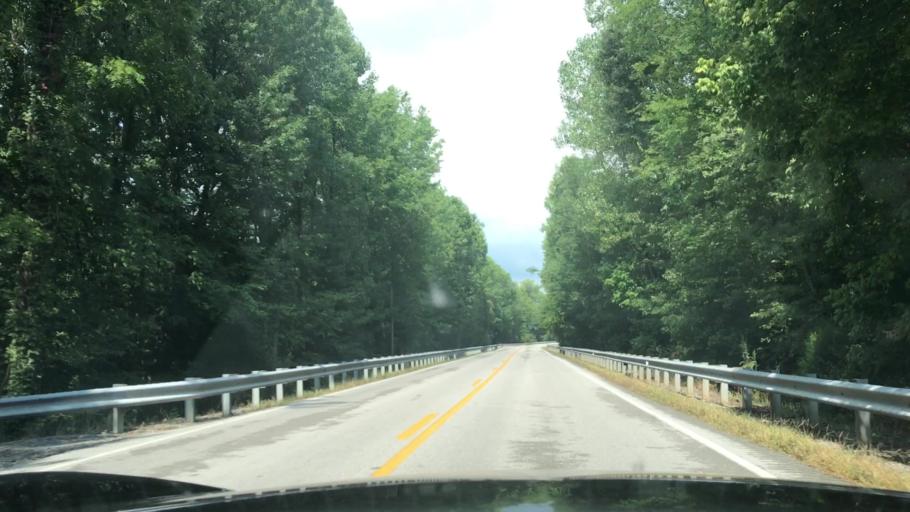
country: US
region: Kentucky
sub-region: Ohio County
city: Beaver Dam
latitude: 37.2078
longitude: -86.8949
